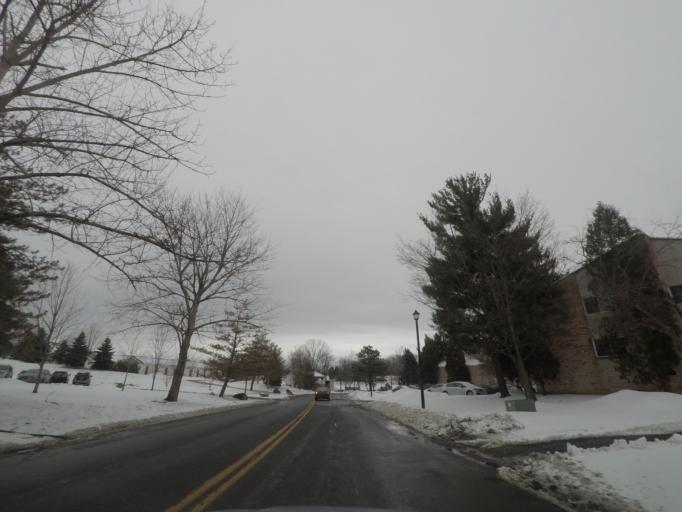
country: US
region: New York
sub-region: Albany County
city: Watervliet
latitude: 42.7334
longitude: -73.7304
